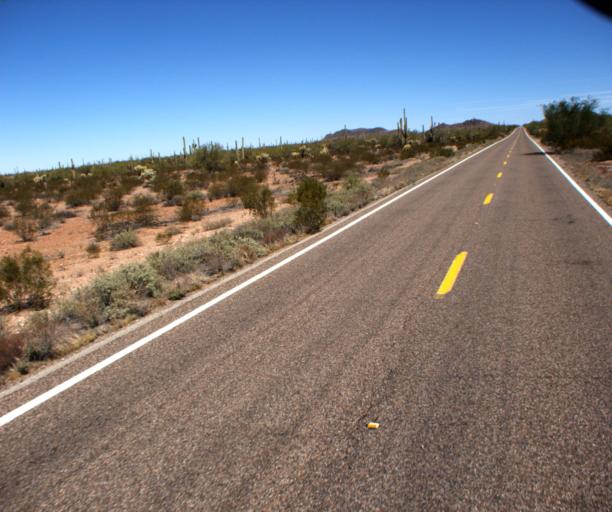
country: MX
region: Sonora
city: Sonoyta
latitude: 32.0523
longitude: -112.7905
